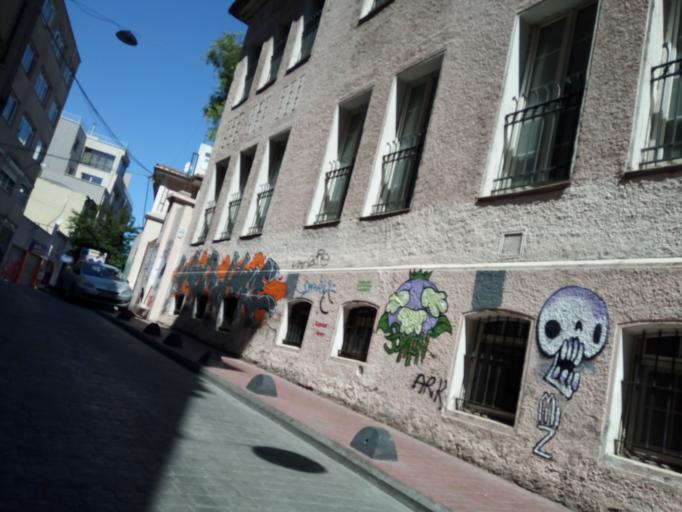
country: TR
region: Istanbul
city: Eminoenue
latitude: 41.0325
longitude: 28.9847
